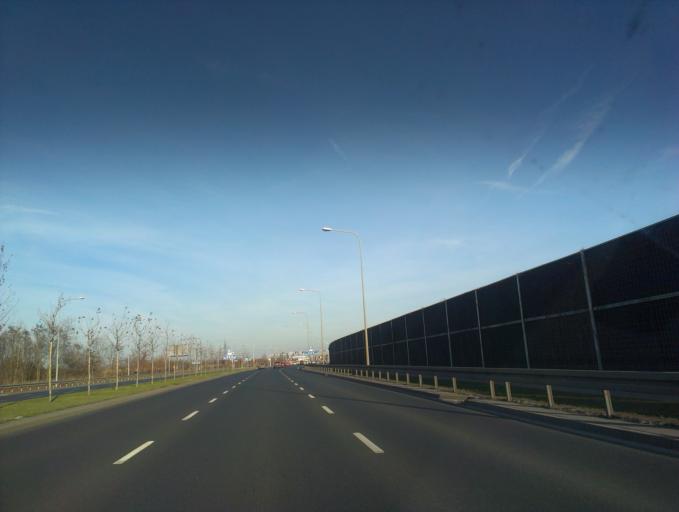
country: PL
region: Greater Poland Voivodeship
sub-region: Poznan
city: Poznan
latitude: 52.4173
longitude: 16.9589
